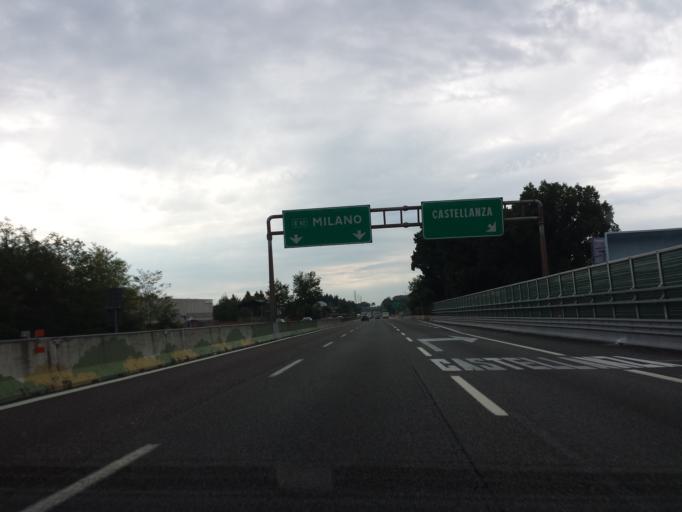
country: IT
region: Lombardy
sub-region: Citta metropolitana di Milano
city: Legnano
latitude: 45.6126
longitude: 8.9224
